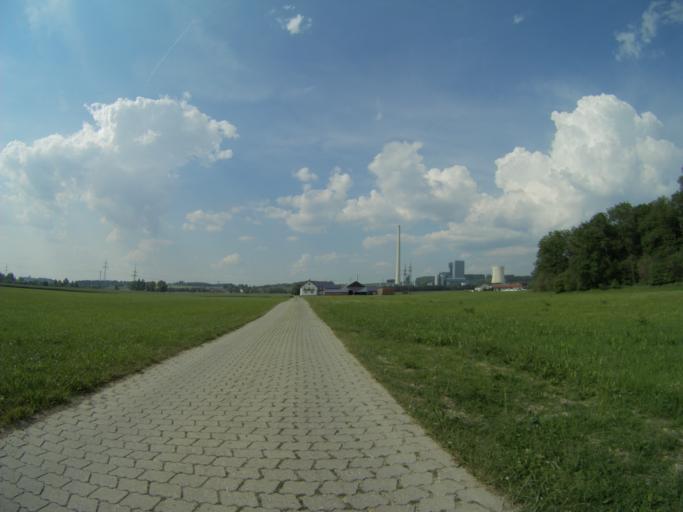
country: DE
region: Bavaria
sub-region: Upper Bavaria
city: Haag an der Amper
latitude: 48.4454
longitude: 11.7992
